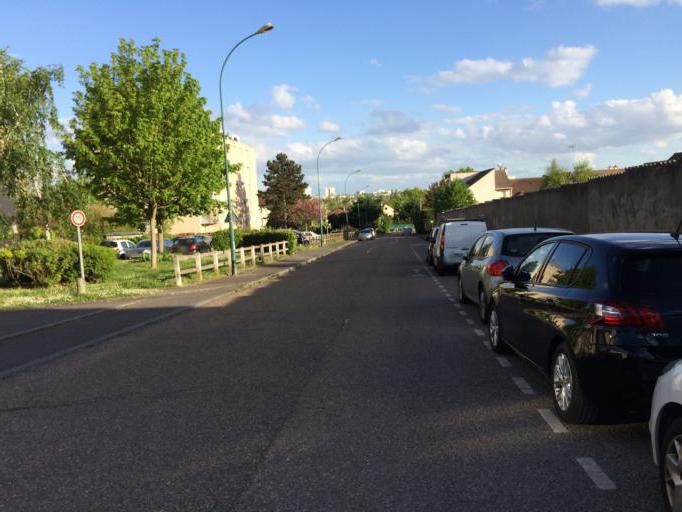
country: FR
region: Ile-de-France
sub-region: Departement de l'Essonne
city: Verrieres-le-Buisson
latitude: 48.7466
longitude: 2.2751
